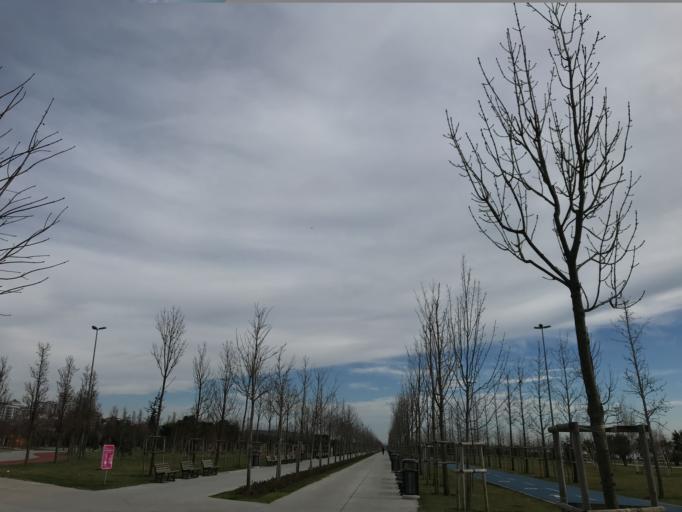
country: TR
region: Istanbul
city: Maltepe
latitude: 40.9358
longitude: 29.1106
